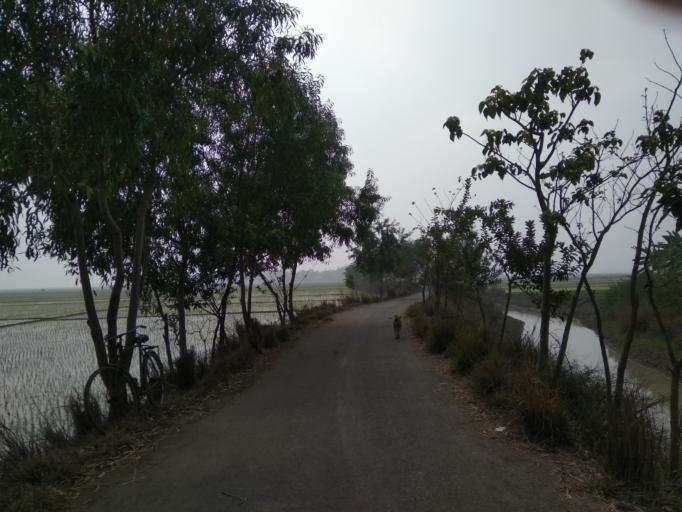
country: BD
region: Rajshahi
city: Bogra
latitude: 24.4728
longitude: 89.2690
